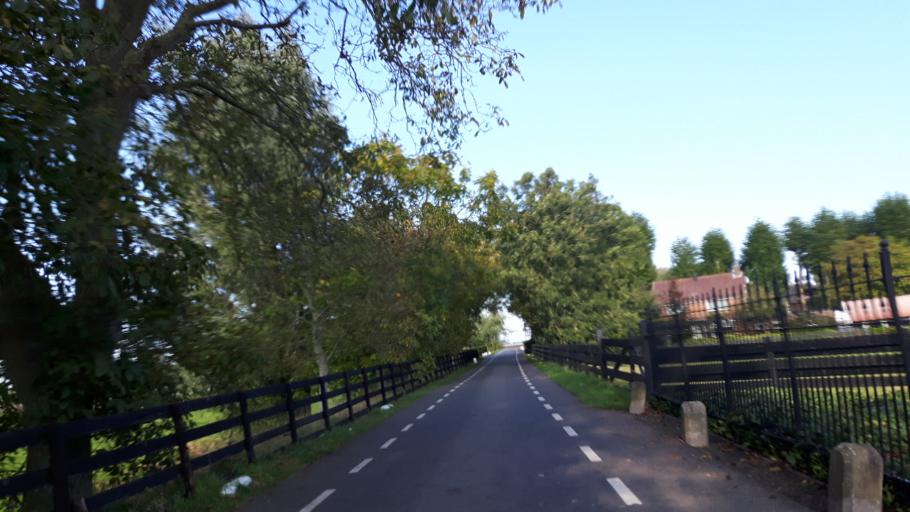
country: NL
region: Utrecht
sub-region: Gemeente Oudewater
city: Oudewater
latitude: 52.0252
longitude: 4.8945
